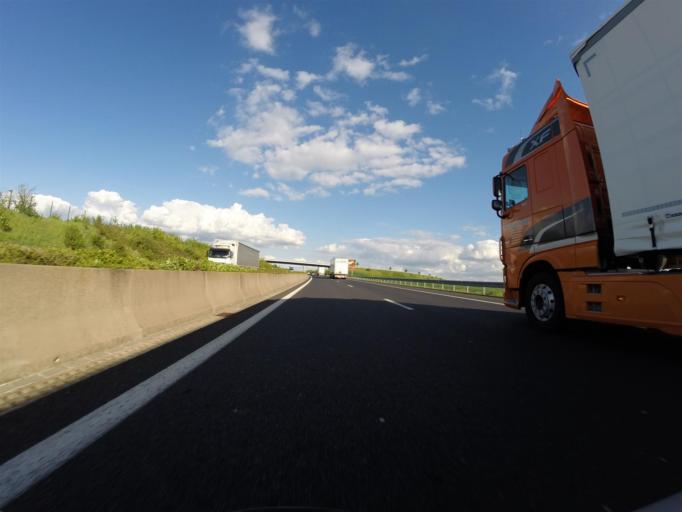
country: LU
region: Grevenmacher
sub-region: Canton de Remich
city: Mondorf-les-Bains
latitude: 49.4953
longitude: 6.3153
